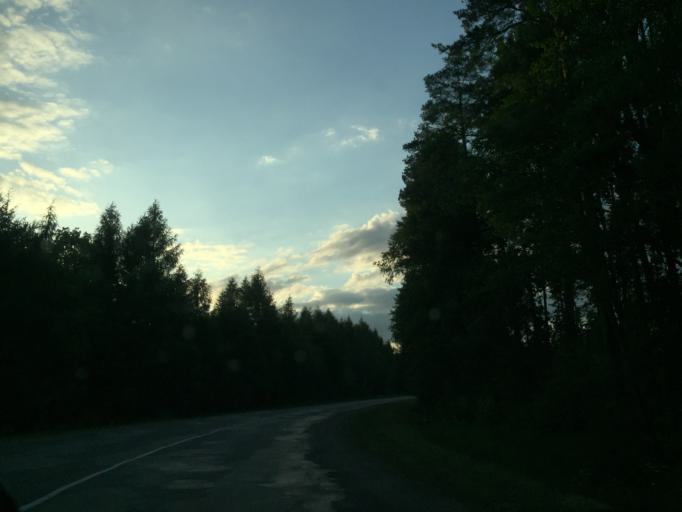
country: LV
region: Sigulda
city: Sigulda
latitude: 57.1114
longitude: 24.9201
